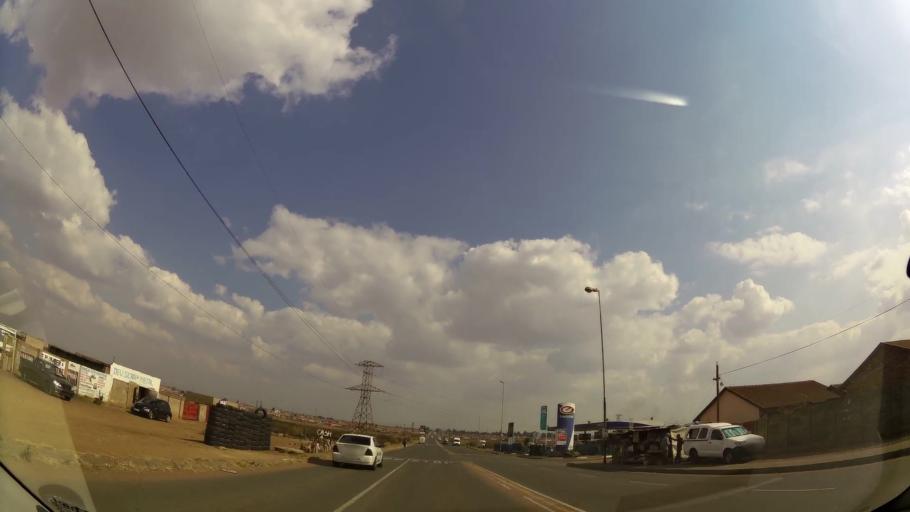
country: ZA
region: Gauteng
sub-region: Ekurhuleni Metropolitan Municipality
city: Springs
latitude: -26.1212
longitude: 28.4571
